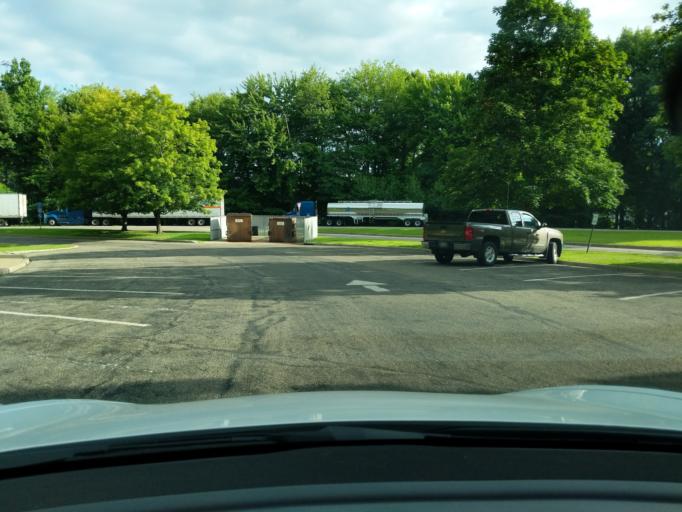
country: US
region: Ohio
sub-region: Ashtabula County
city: Conneaut
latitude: 41.9420
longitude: -80.4726
